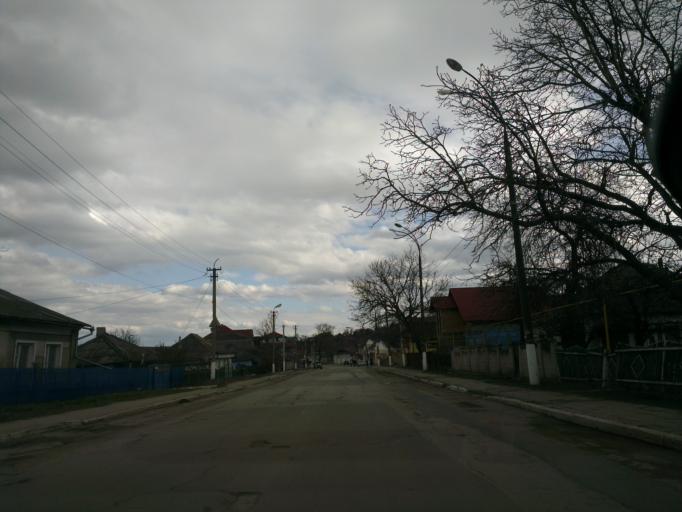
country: MD
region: Hincesti
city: Hincesti
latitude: 46.8213
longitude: 28.5983
